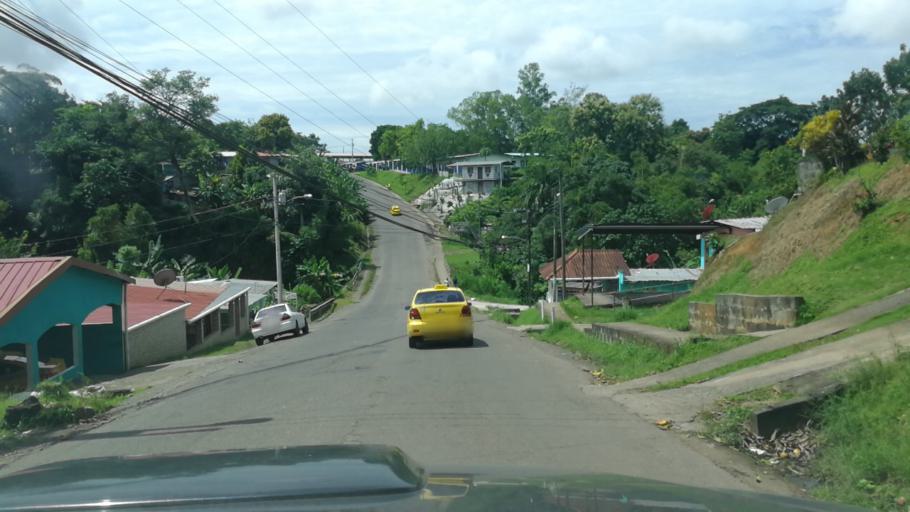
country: PA
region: Panama
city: Tocumen
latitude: 9.0961
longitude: -79.4087
